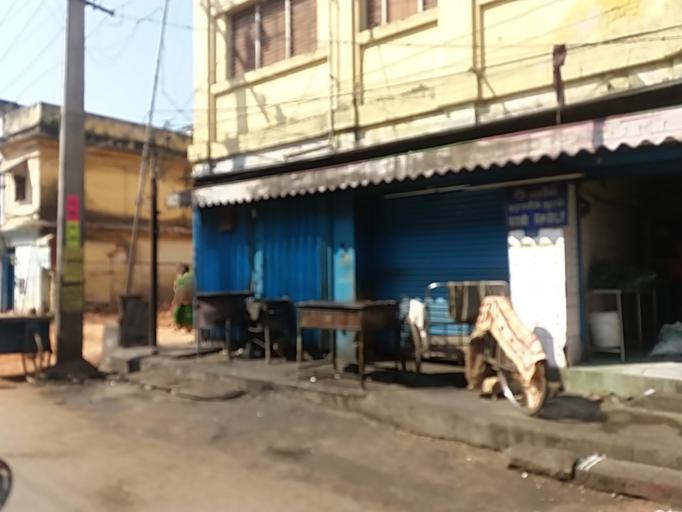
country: IN
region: Tamil Nadu
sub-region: Tiruchchirappalli
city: Tiruchirappalli
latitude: 10.8274
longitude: 78.6999
